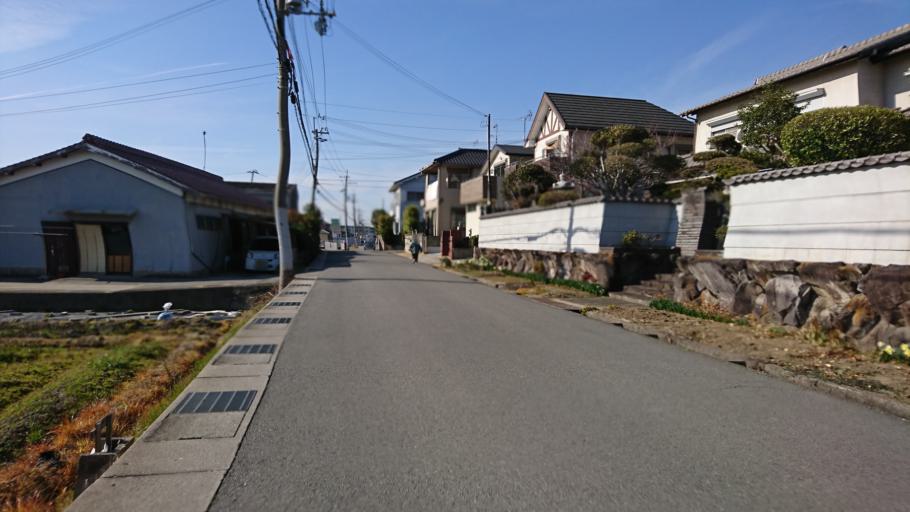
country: JP
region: Hyogo
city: Kakogawacho-honmachi
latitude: 34.7316
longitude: 134.8716
